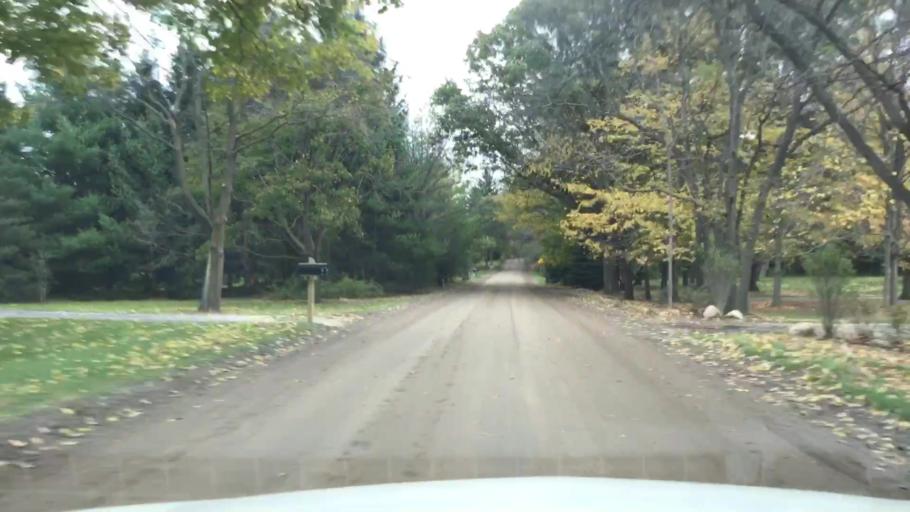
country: US
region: Michigan
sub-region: Oakland County
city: Rochester
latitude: 42.7482
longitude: -83.1110
